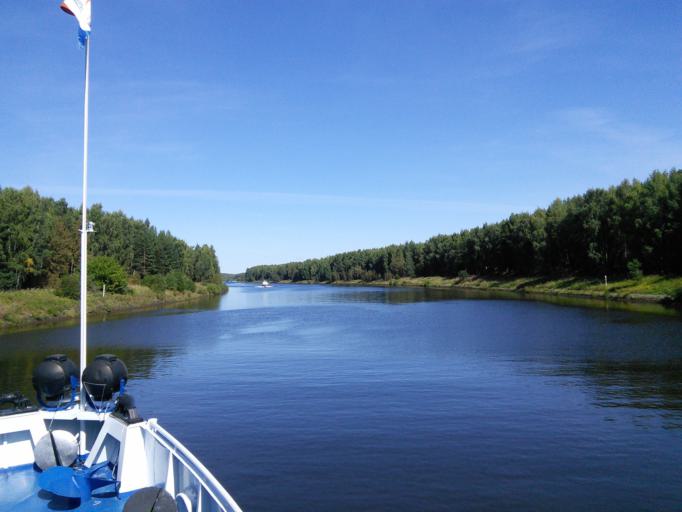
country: RU
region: Moskovskaya
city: Pirogovskiy
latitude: 56.0296
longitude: 37.6650
